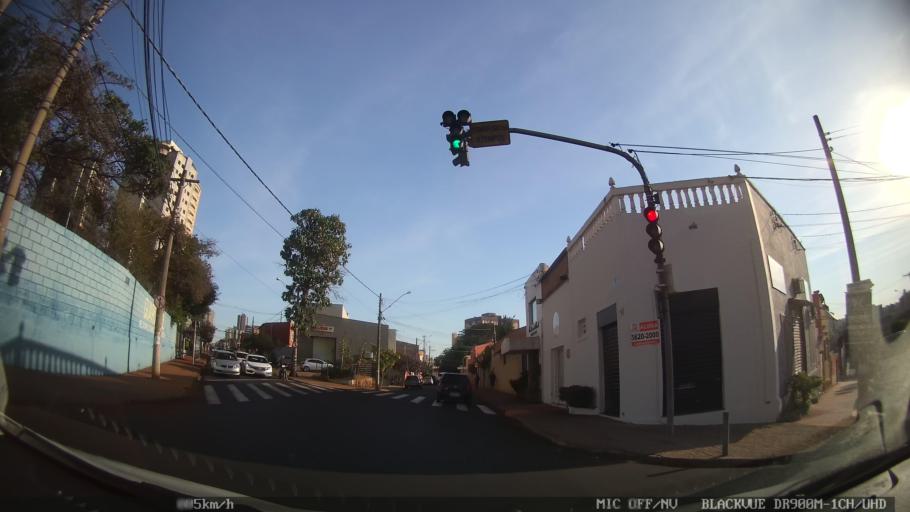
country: BR
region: Sao Paulo
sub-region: Ribeirao Preto
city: Ribeirao Preto
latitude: -21.1858
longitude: -47.8016
